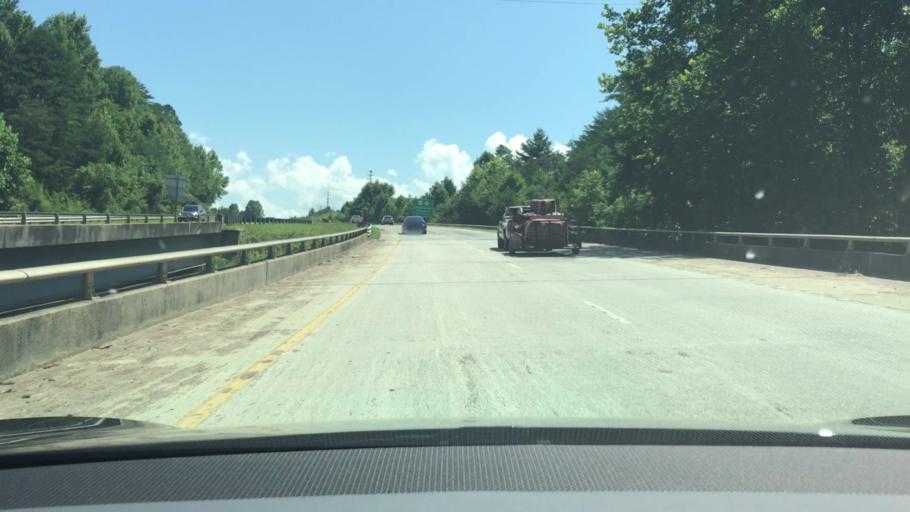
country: US
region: North Carolina
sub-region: Macon County
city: Franklin
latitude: 35.1640
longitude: -83.3754
